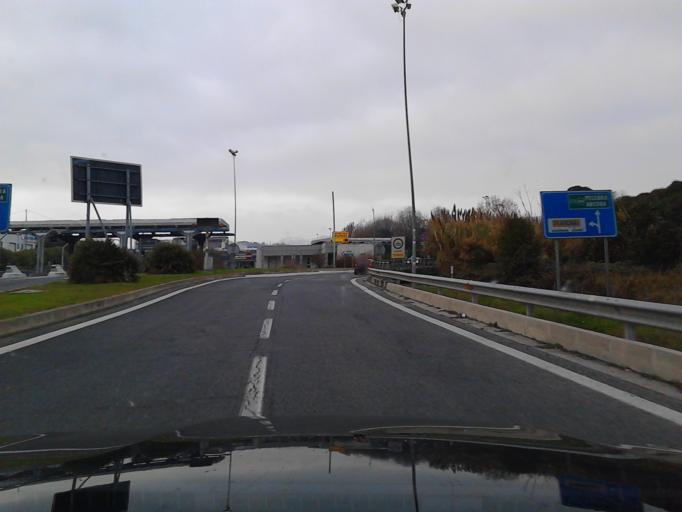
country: IT
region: Abruzzo
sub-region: Provincia di Teramo
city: Alba Adriatica
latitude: 42.8345
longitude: 13.9030
